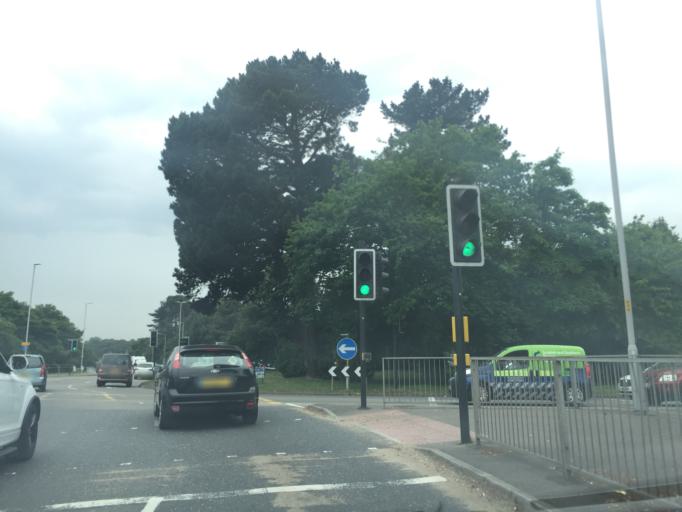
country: GB
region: England
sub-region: Dorset
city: Parkstone
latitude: 50.7544
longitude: -1.9314
